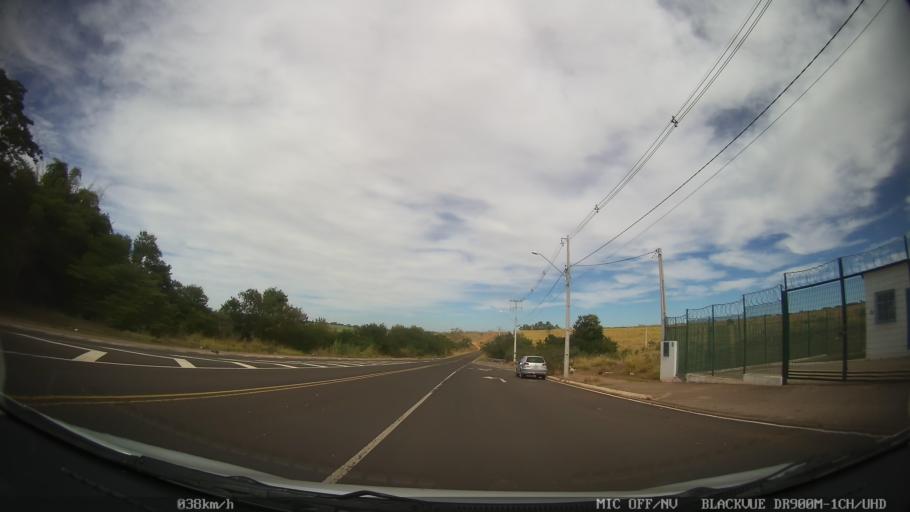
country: BR
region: Sao Paulo
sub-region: Catanduva
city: Catanduva
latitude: -21.1702
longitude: -48.9620
